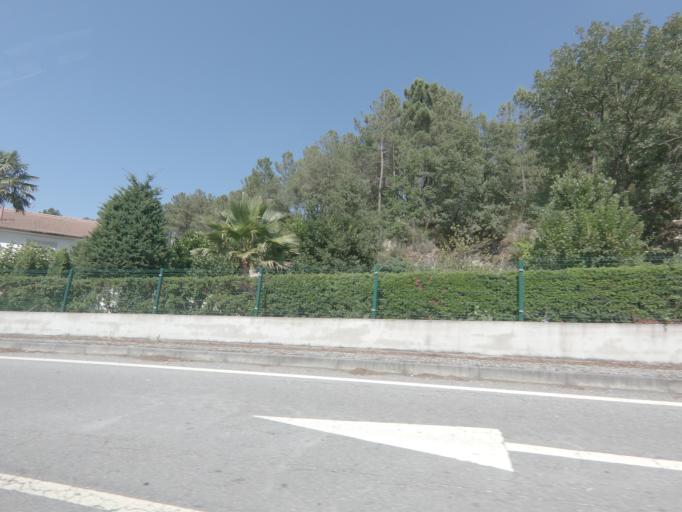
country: PT
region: Viseu
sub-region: Tarouca
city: Tarouca
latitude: 41.0237
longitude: -7.7519
